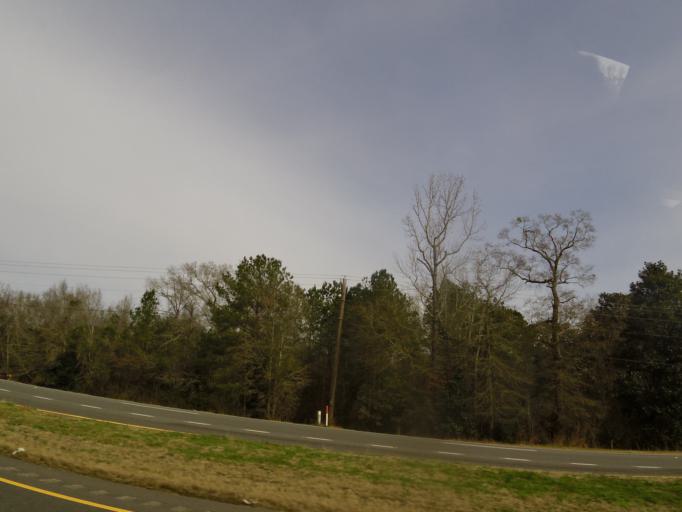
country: US
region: Alabama
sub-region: Dale County
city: Ozark
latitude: 31.4645
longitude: -85.6731
